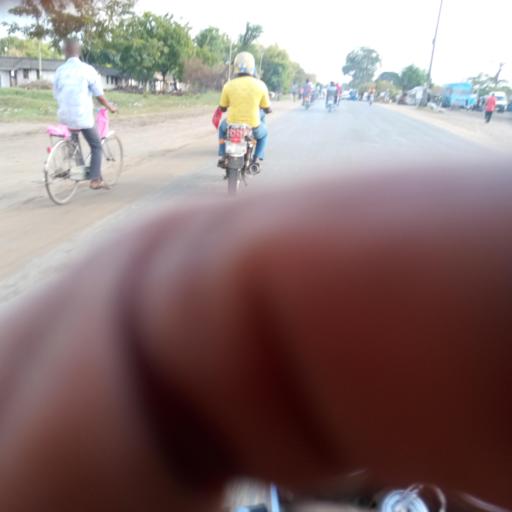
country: TZ
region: Tanga
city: Tanga
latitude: -5.0940
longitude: 39.0960
